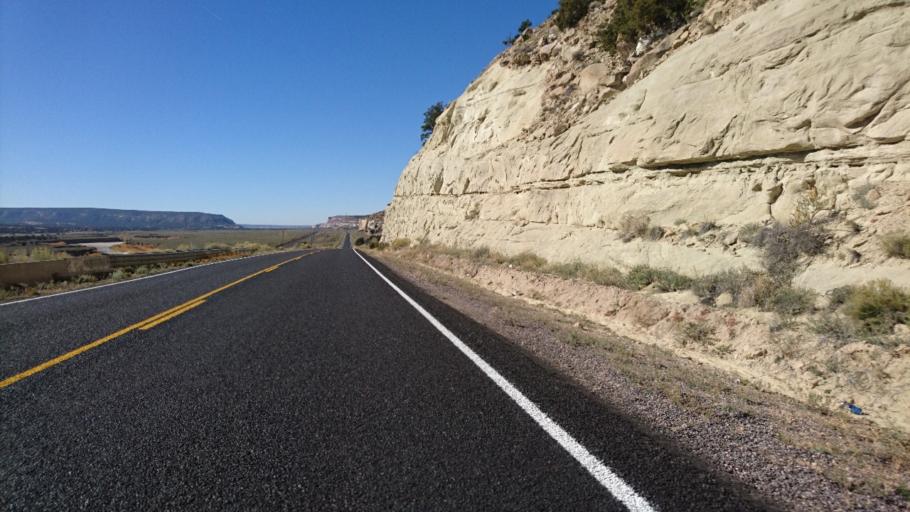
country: US
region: Arizona
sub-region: Apache County
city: Houck
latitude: 35.4123
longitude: -109.0024
